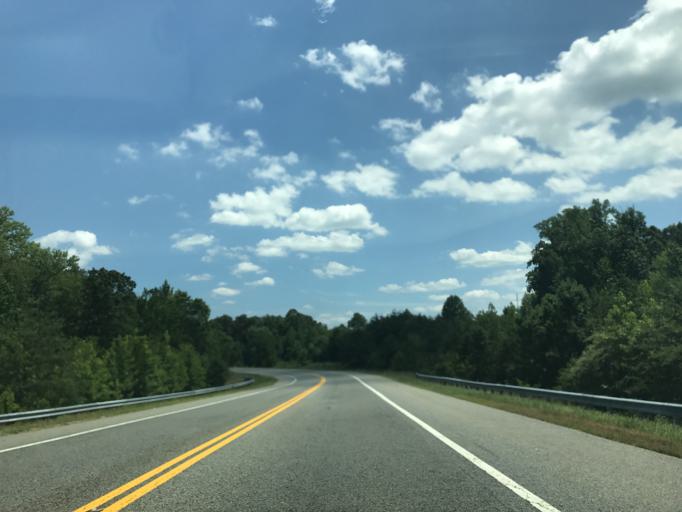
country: US
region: Maryland
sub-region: Prince George's County
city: Glenn Dale
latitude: 39.0290
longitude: -76.7780
